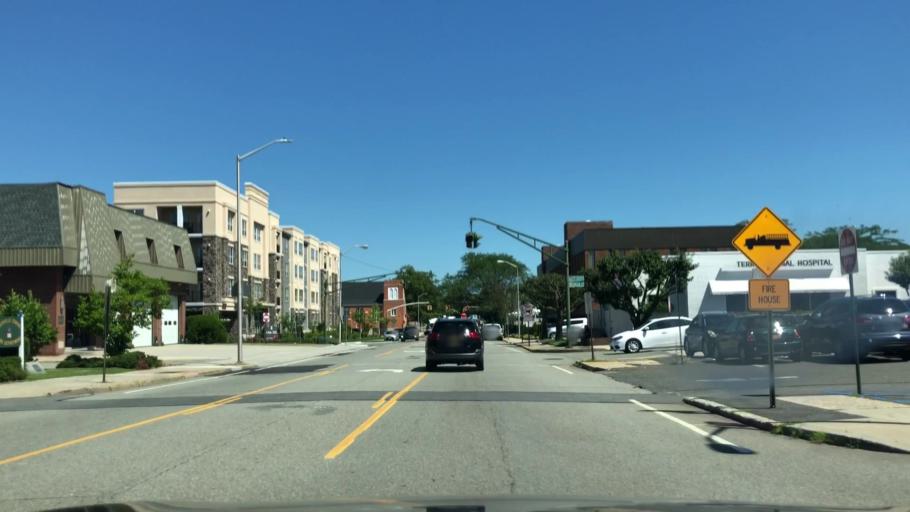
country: US
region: New York
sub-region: Nassau County
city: Rockville Centre
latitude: 40.6586
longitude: -73.6495
